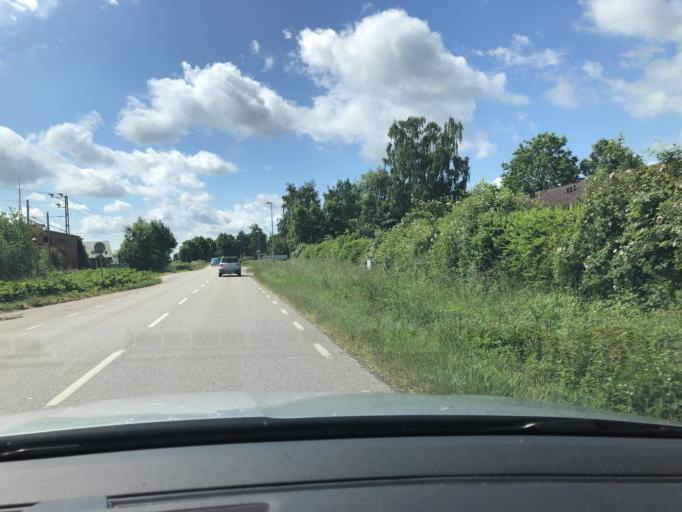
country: SE
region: Blekinge
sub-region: Solvesborgs Kommun
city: Soelvesborg
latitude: 56.1078
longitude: 14.6197
